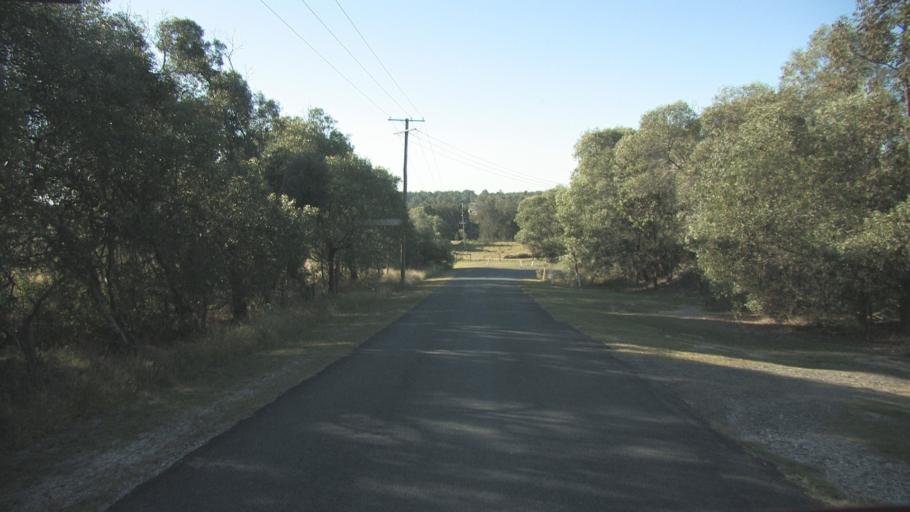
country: AU
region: Queensland
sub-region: Logan
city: Chambers Flat
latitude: -27.7581
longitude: 153.1239
